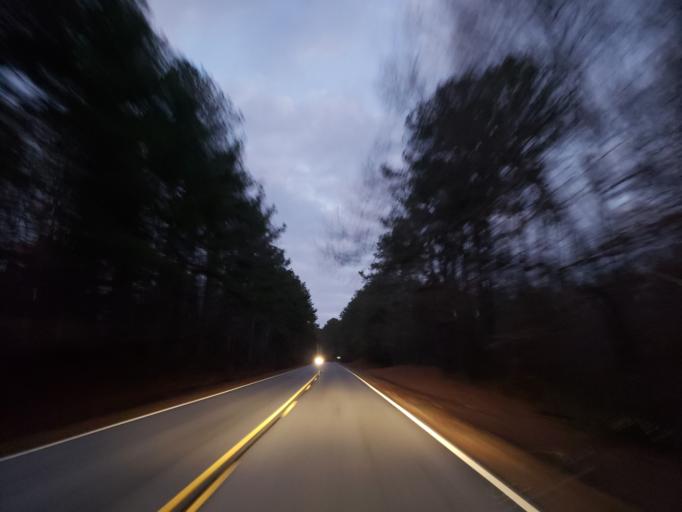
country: US
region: Georgia
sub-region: Carroll County
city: Temple
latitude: 33.8184
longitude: -85.0444
